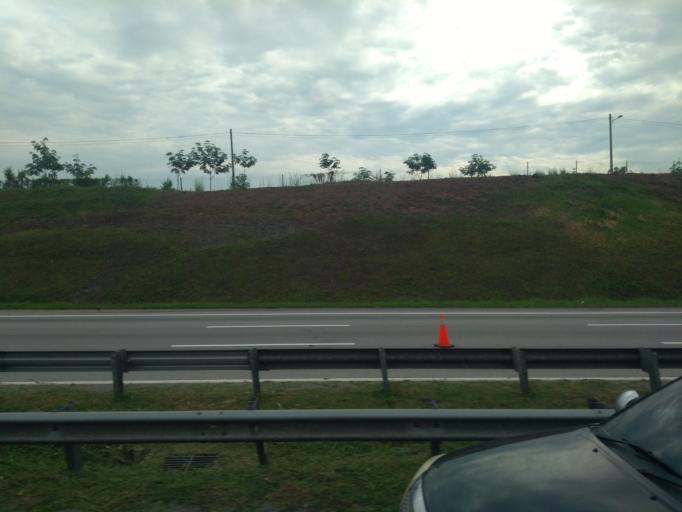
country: MY
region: Melaka
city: Pulau Sebang
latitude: 2.4196
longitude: 102.2157
